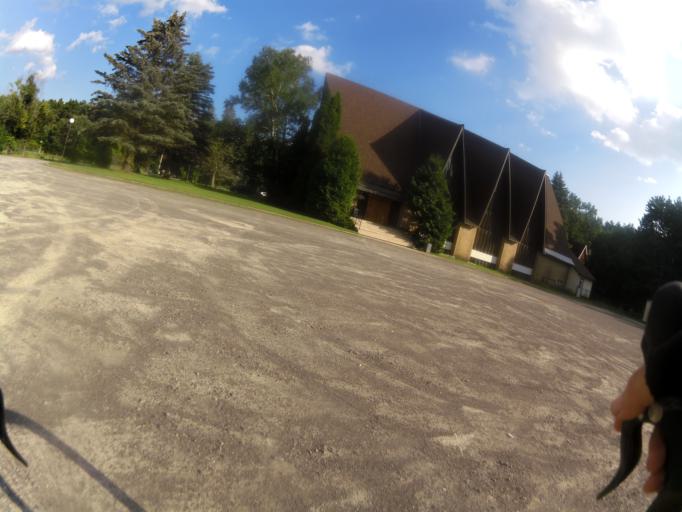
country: CA
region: Ontario
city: Ottawa
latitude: 45.3235
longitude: -75.7279
